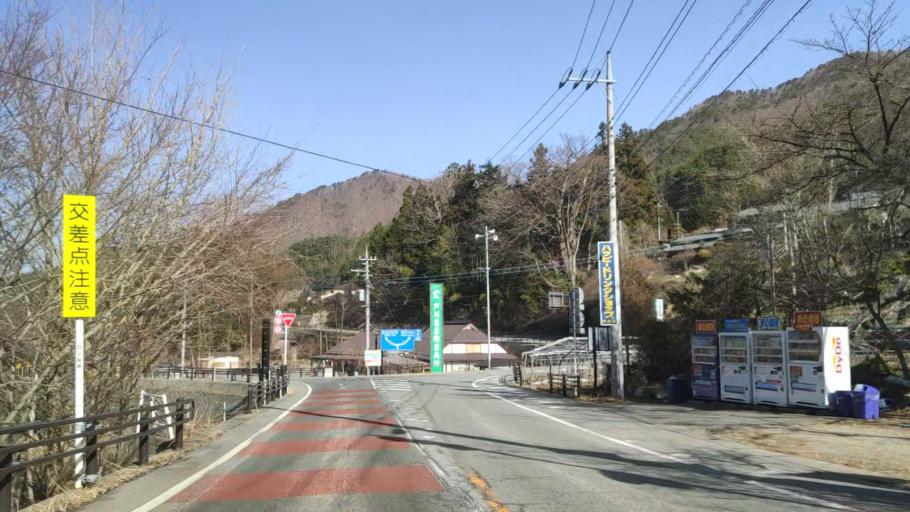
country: JP
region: Yamanashi
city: Fujikawaguchiko
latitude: 35.5520
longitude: 138.6895
